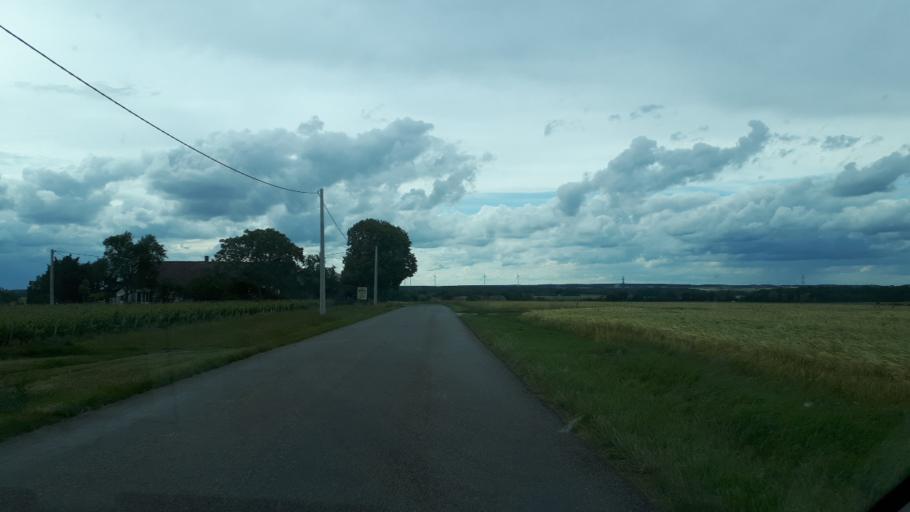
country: FR
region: Centre
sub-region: Departement de l'Indre
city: Reuilly
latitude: 47.0909
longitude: 2.0210
